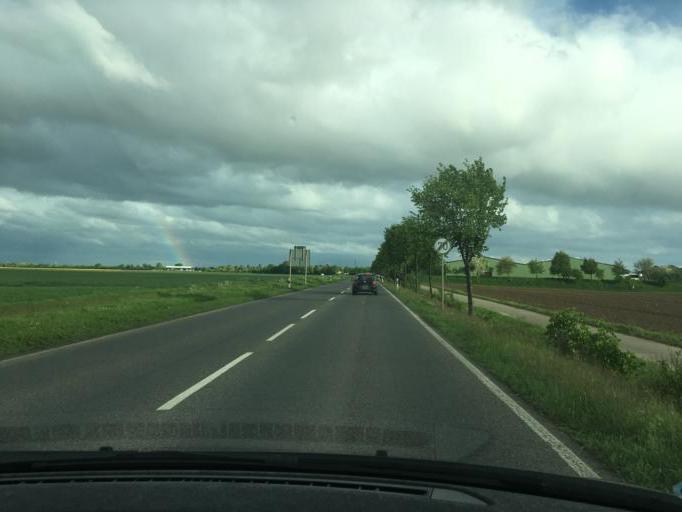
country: DE
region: North Rhine-Westphalia
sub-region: Regierungsbezirk Koln
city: Merzenich
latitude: 50.8220
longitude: 6.5438
